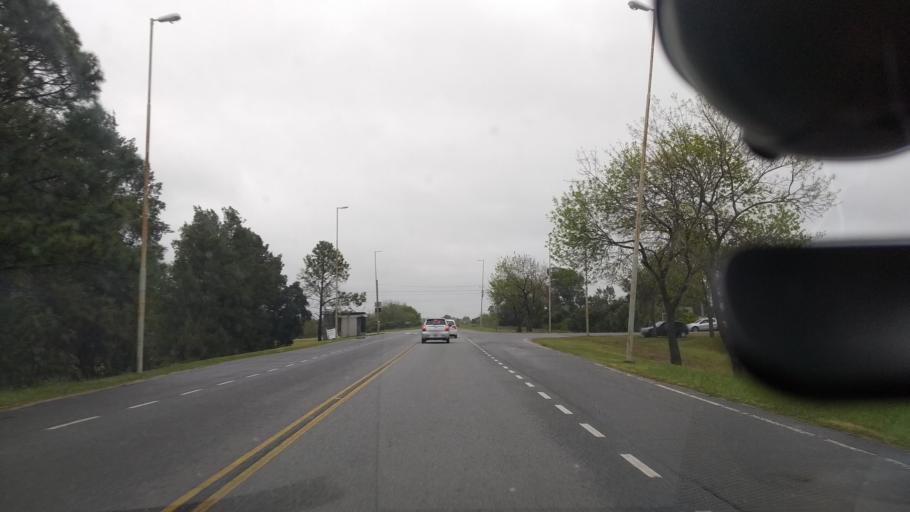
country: AR
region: Buenos Aires
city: Veronica
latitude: -35.4006
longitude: -57.3536
